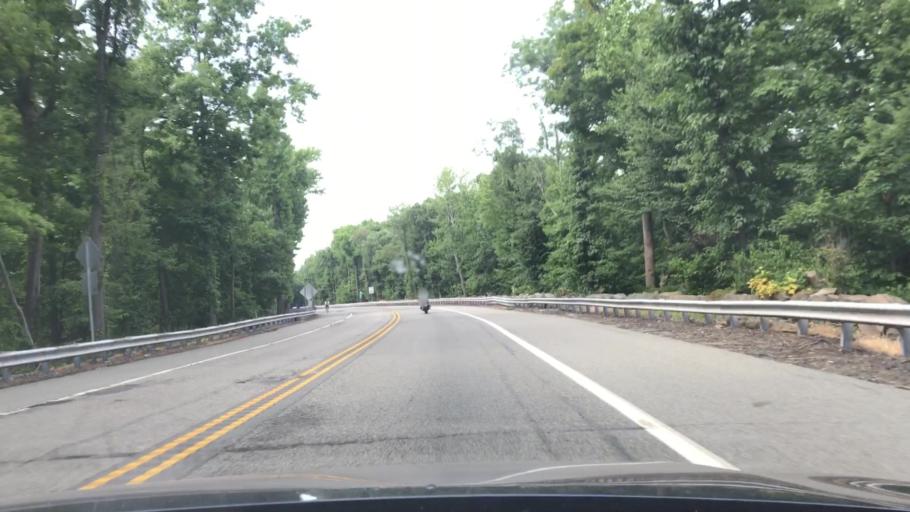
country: US
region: New Jersey
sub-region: Bergen County
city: Tenafly
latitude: 40.9157
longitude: -73.9365
